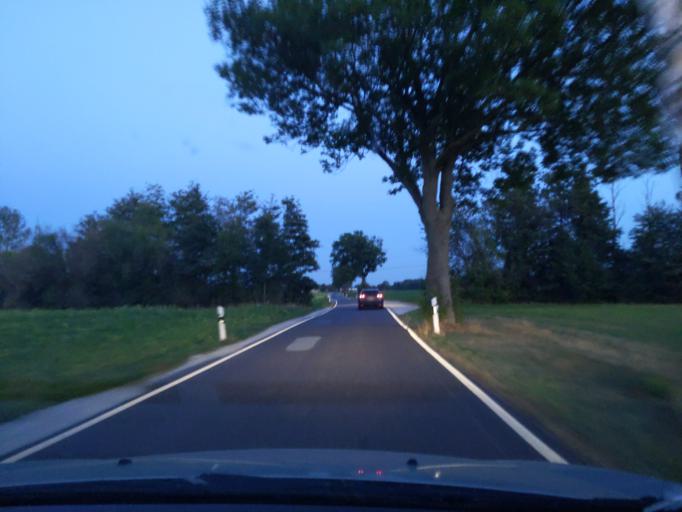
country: DE
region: Saxony
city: Grossdubrau
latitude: 51.3010
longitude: 14.4393
